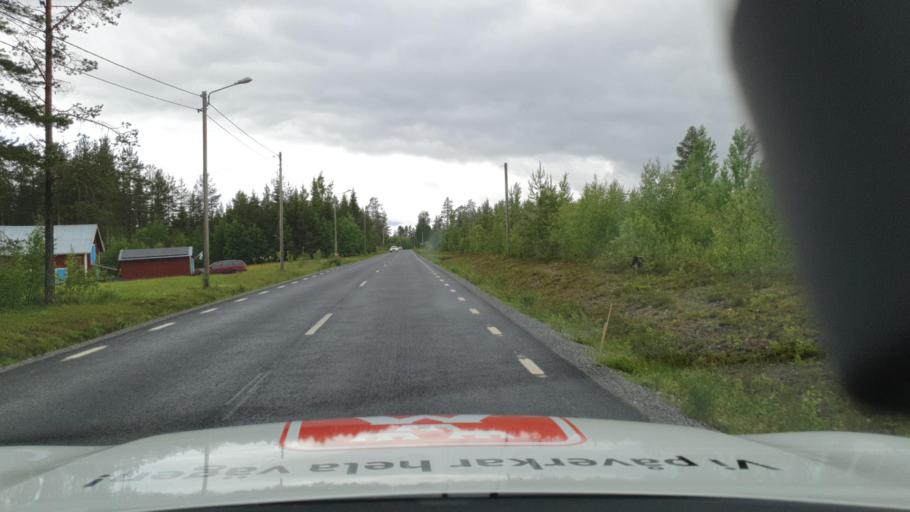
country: SE
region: Vaesterbotten
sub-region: Dorotea Kommun
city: Dorotea
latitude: 64.2148
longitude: 16.5503
